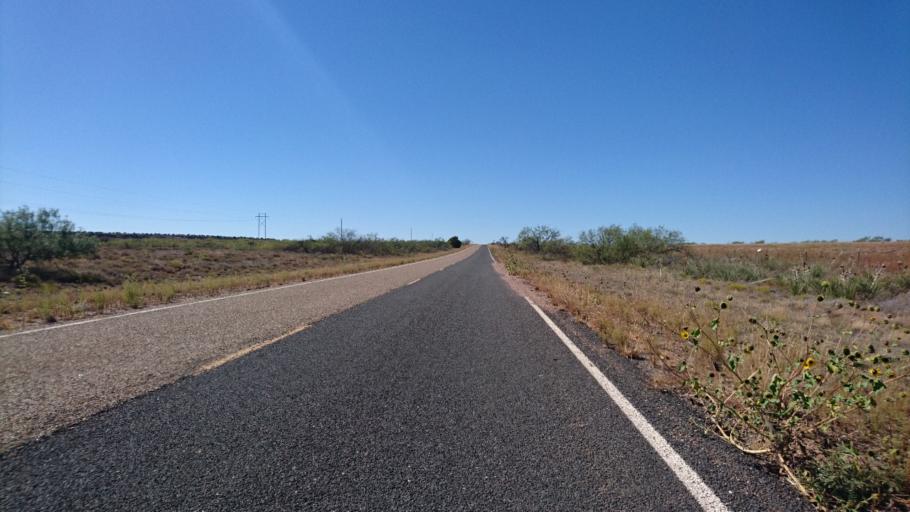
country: US
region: New Mexico
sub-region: Quay County
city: Tucumcari
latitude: 35.0808
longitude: -104.1195
